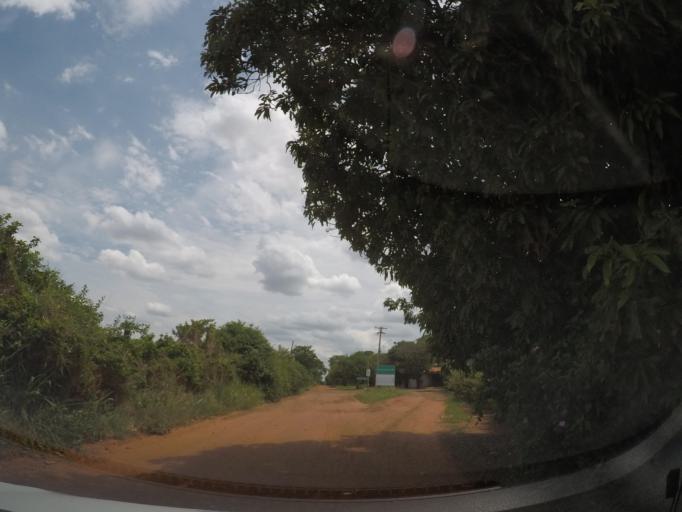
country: BR
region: Sao Paulo
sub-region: Sumare
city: Sumare
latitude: -22.8470
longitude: -47.2930
